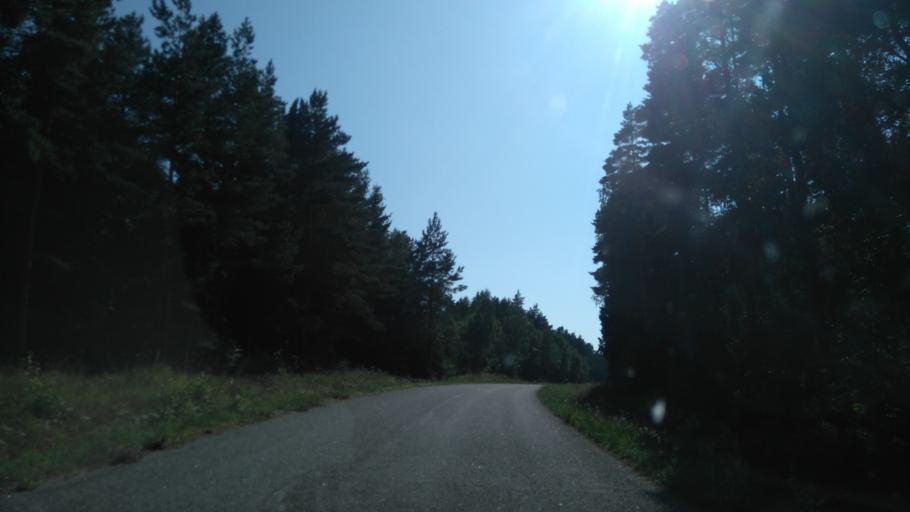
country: EE
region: Saare
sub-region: Kuressaare linn
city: Kuressaare
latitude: 58.5746
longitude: 22.4313
